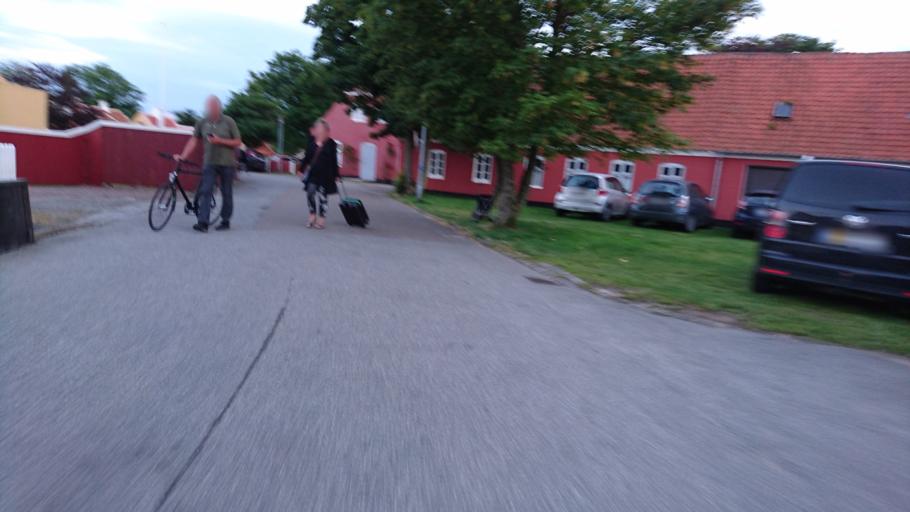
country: DK
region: North Denmark
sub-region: Frederikshavn Kommune
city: Skagen
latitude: 57.7251
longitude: 10.5995
